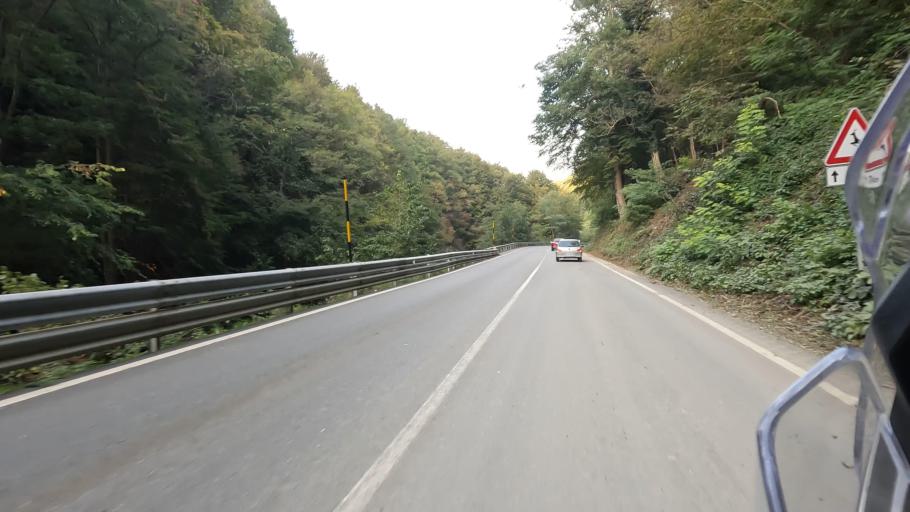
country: IT
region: Liguria
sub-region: Provincia di Savona
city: Sassello
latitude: 44.4591
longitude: 8.4801
